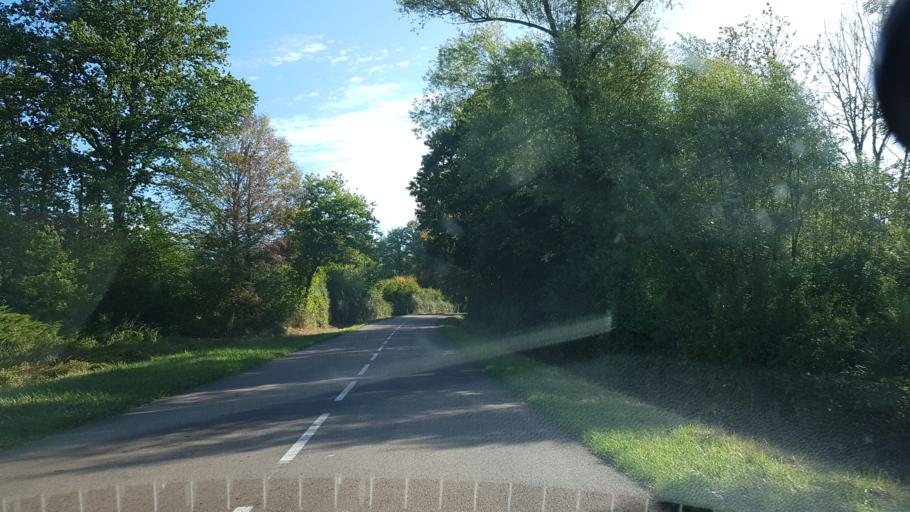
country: FR
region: Bourgogne
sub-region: Departement de la Nievre
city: Saint-Amand-en-Puisaye
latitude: 47.5334
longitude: 3.0483
